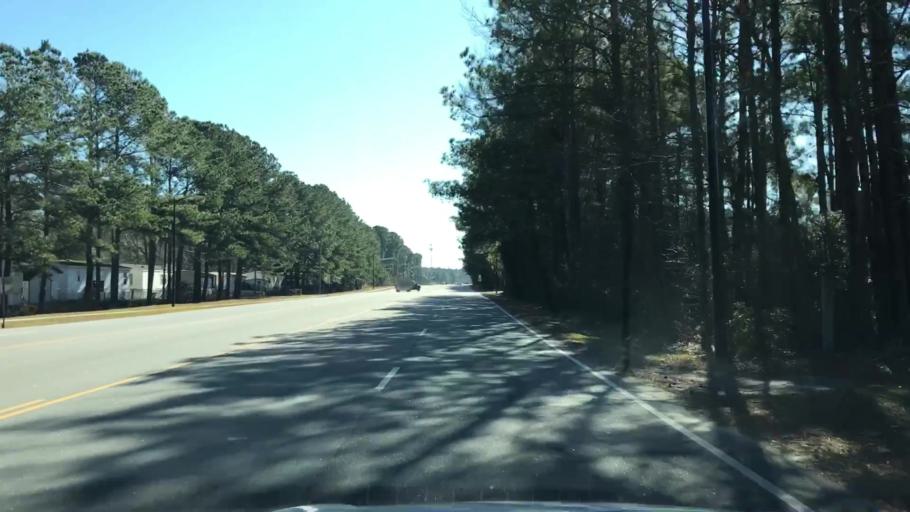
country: US
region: South Carolina
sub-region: Berkeley County
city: Ladson
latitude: 32.9218
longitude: -80.1089
